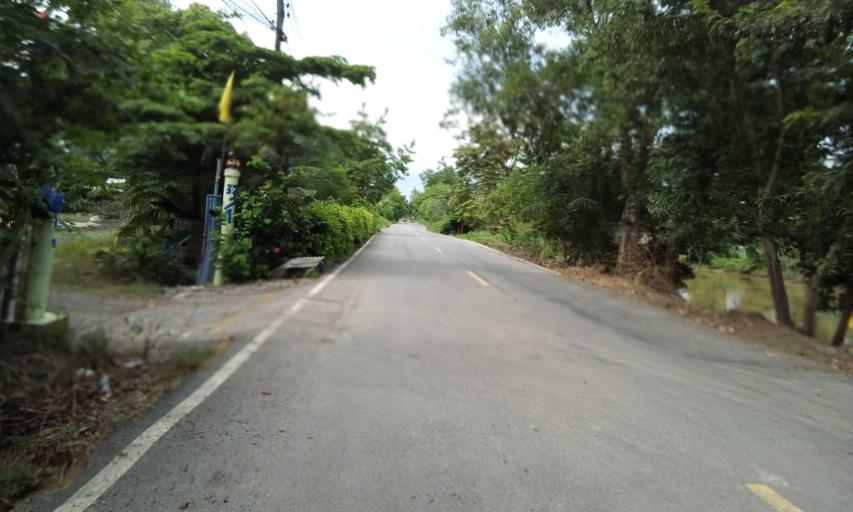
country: TH
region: Pathum Thani
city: Nong Suea
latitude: 14.1723
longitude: 100.8231
